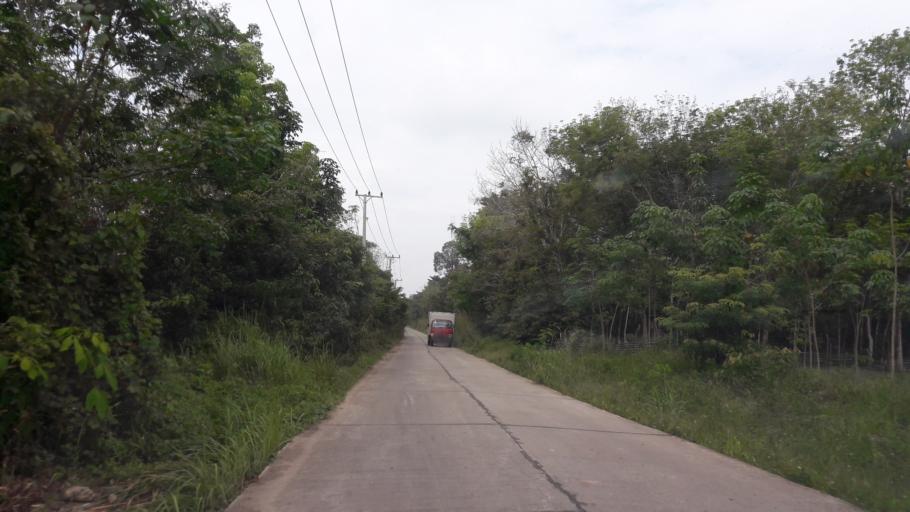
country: ID
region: South Sumatra
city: Gunungmenang
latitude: -3.2385
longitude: 104.1258
